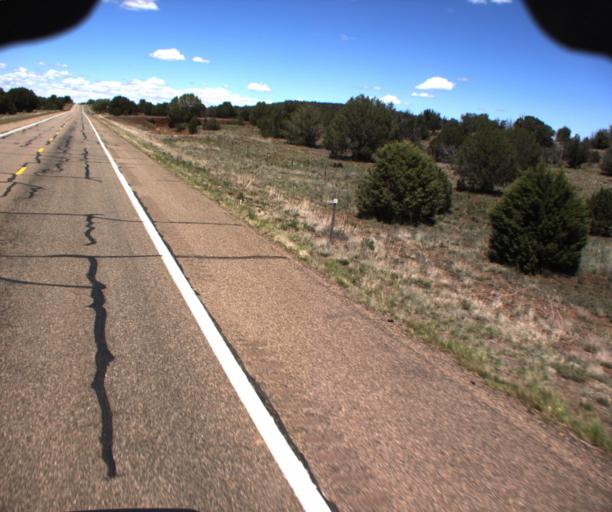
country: US
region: Arizona
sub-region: Yavapai County
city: Paulden
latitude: 35.1259
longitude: -112.4363
